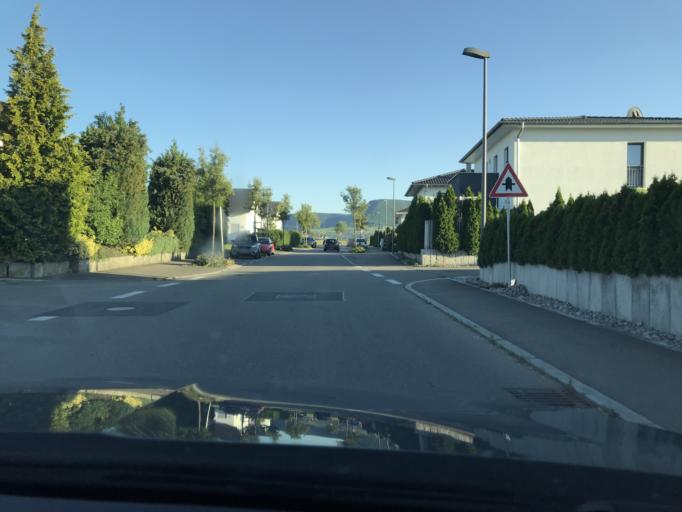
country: DE
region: Baden-Wuerttemberg
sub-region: Regierungsbezirk Stuttgart
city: Dettingen unter Teck
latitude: 48.6096
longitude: 9.4511
